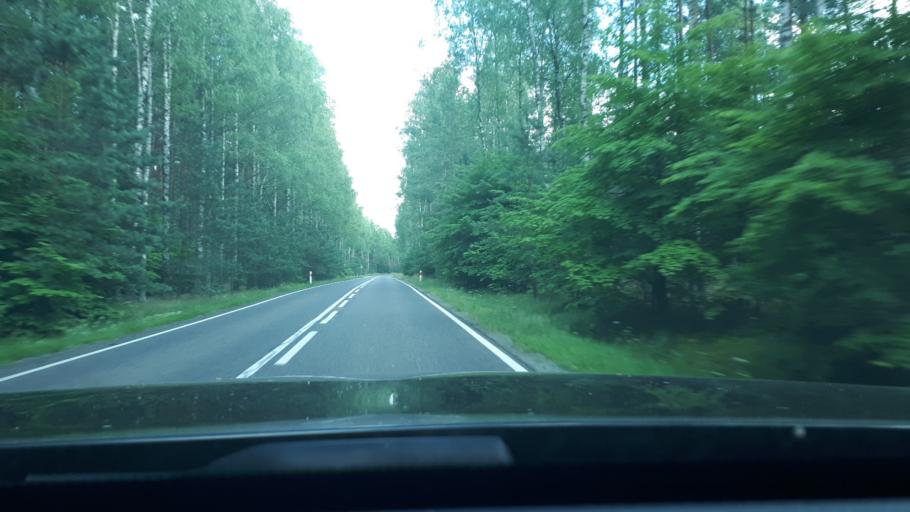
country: PL
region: Warmian-Masurian Voivodeship
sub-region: Powiat olsztynski
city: Stawiguda
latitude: 53.5338
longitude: 20.4337
